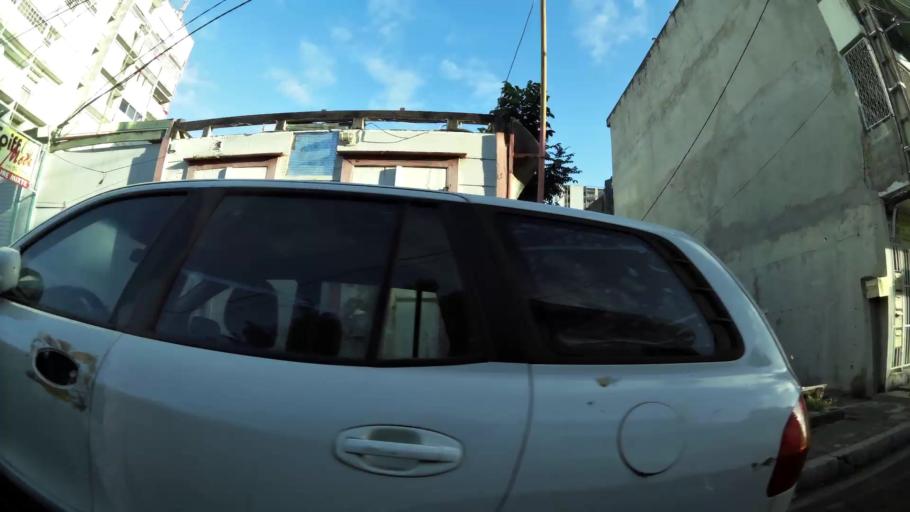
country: GP
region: Guadeloupe
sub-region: Guadeloupe
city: Pointe-a-Pitre
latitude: 16.2406
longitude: -61.5378
